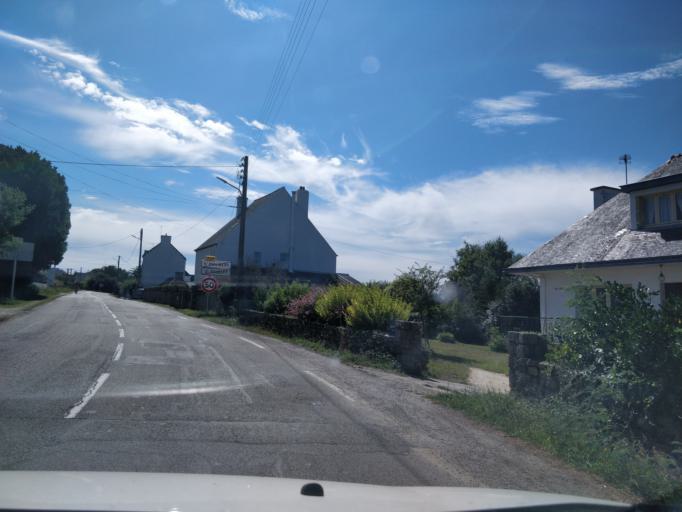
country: FR
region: Brittany
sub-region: Departement du Morbihan
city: Saint-Philibert
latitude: 47.5829
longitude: -2.9998
